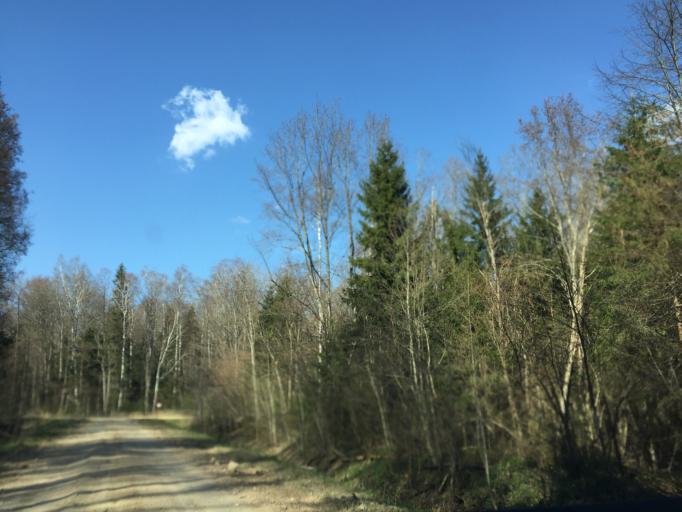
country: LV
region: Lielvarde
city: Lielvarde
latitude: 56.8541
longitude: 24.8041
